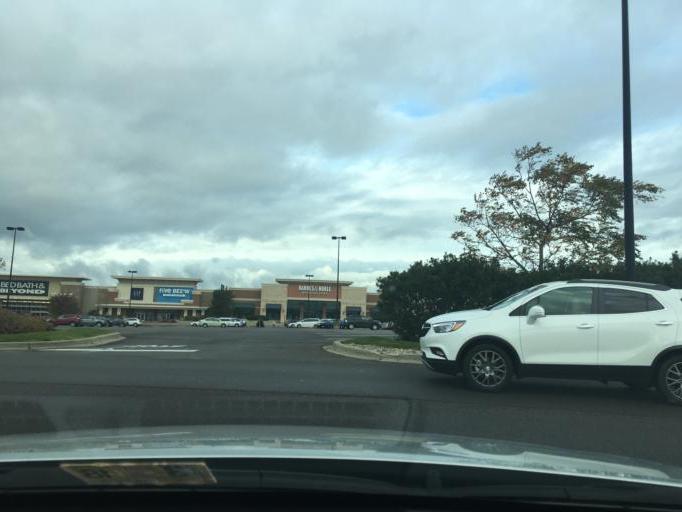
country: US
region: Michigan
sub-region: Wayne County
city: Allen Park
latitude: 42.2834
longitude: -83.2058
